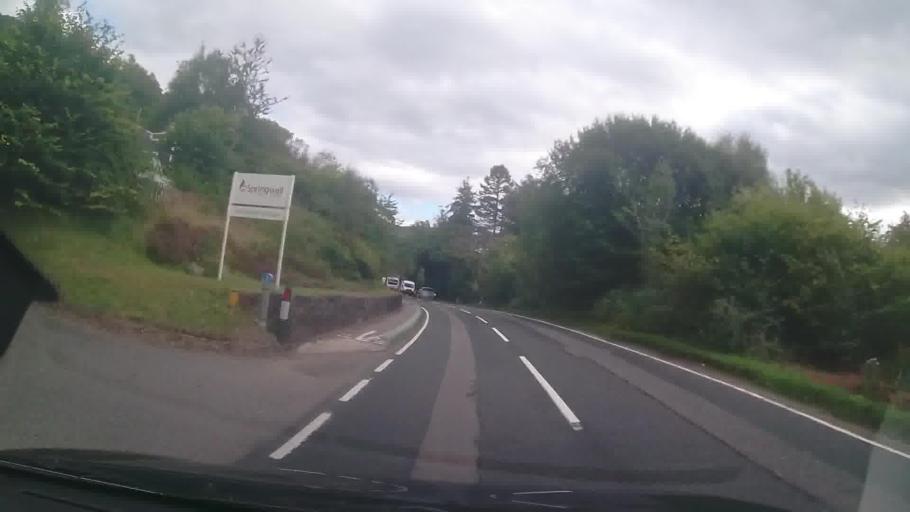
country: GB
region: Scotland
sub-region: Highland
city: Fort William
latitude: 56.7029
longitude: -5.2128
